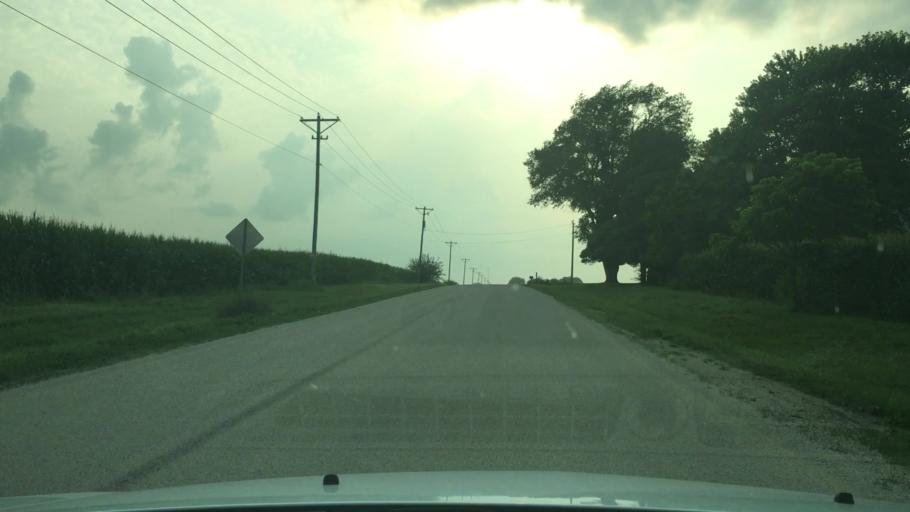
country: US
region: Illinois
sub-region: Ogle County
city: Rochelle
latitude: 41.9203
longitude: -89.0029
